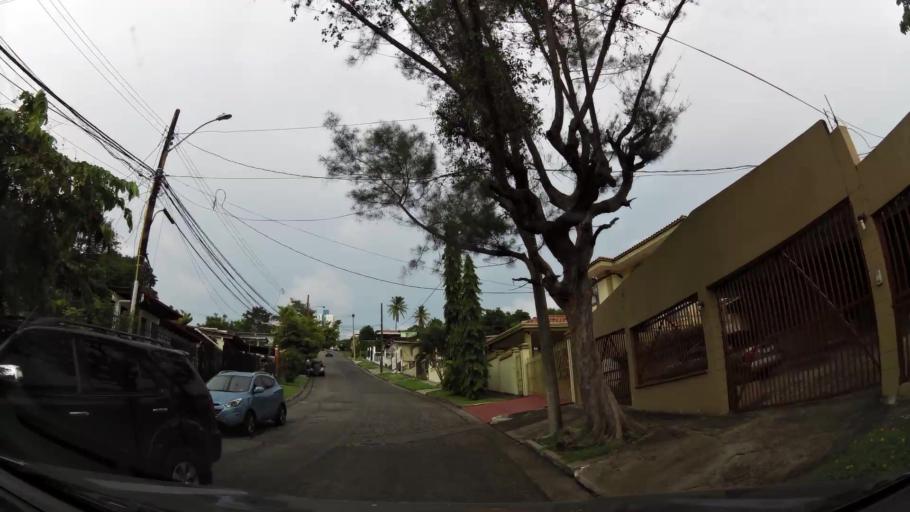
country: PA
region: Panama
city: Panama
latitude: 9.0073
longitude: -79.5315
